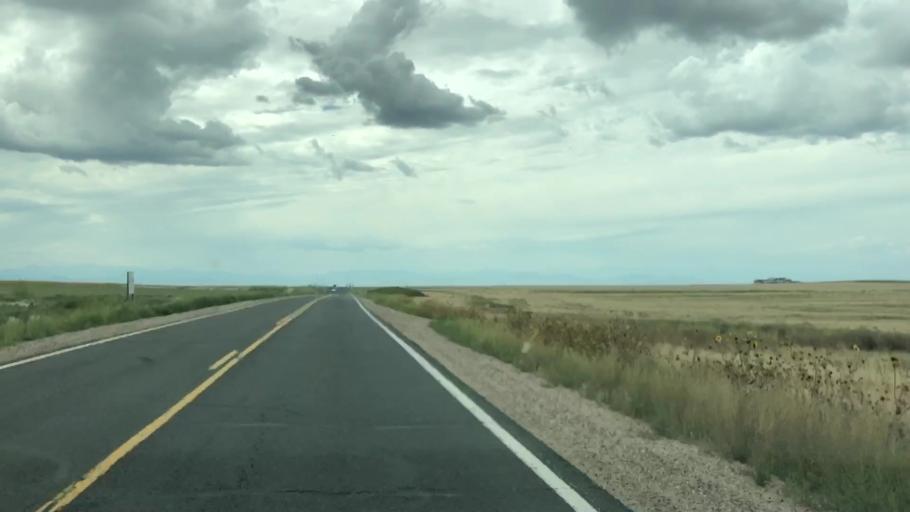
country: US
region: Colorado
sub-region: Adams County
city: Aurora
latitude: 39.7983
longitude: -104.7058
